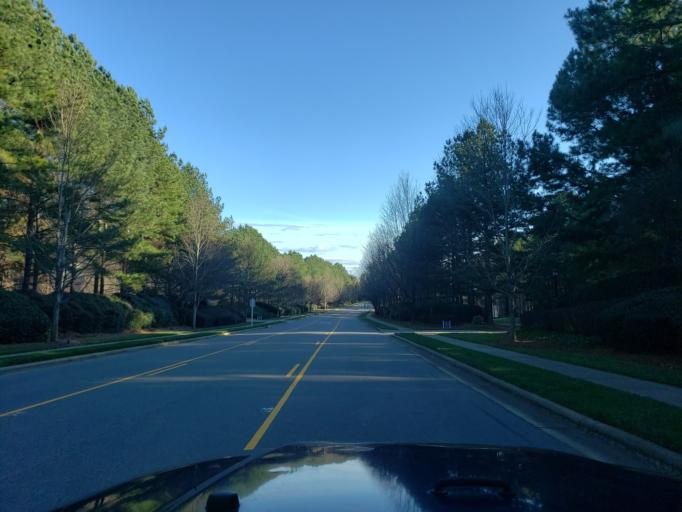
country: US
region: North Carolina
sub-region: Catawba County
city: Lake Norman of Catawba
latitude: 35.5458
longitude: -80.9198
